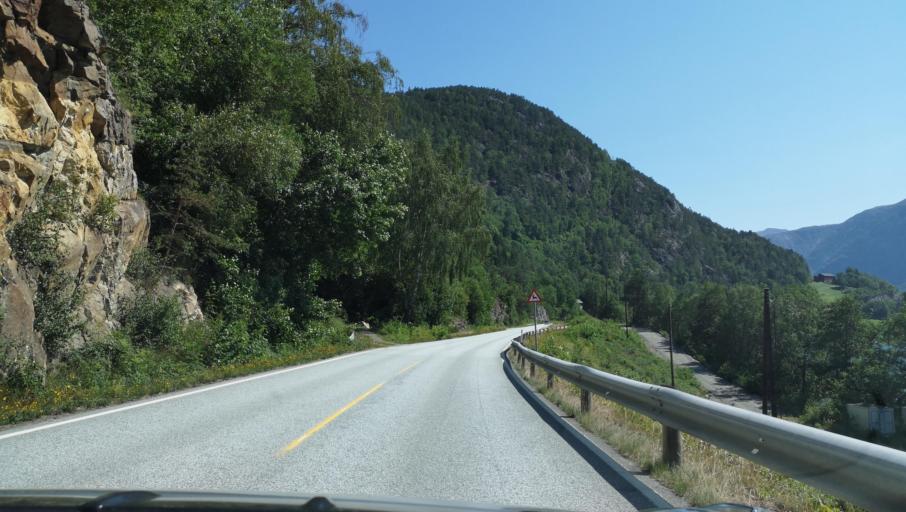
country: NO
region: Hordaland
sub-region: Ulvik
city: Ulvik
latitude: 60.4907
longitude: 6.8580
